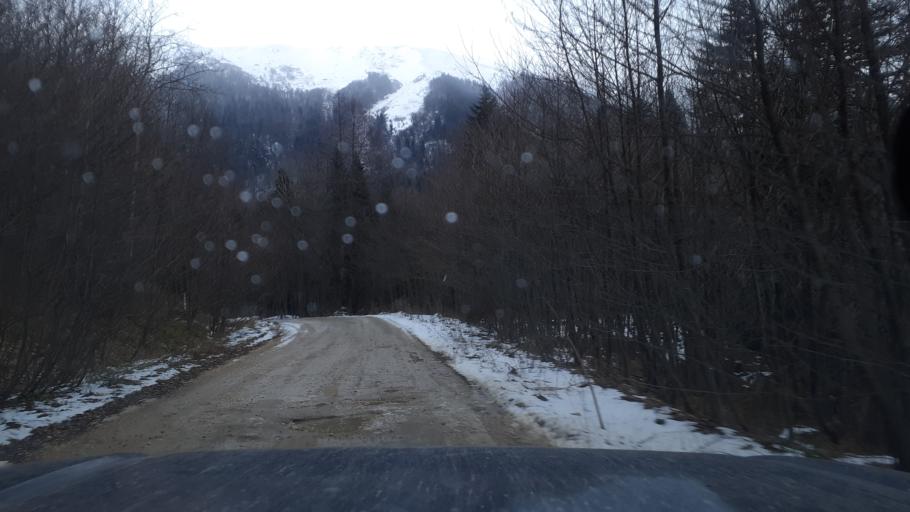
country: RU
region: Krasnodarskiy
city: Neftegorsk
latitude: 44.0780
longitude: 39.8016
